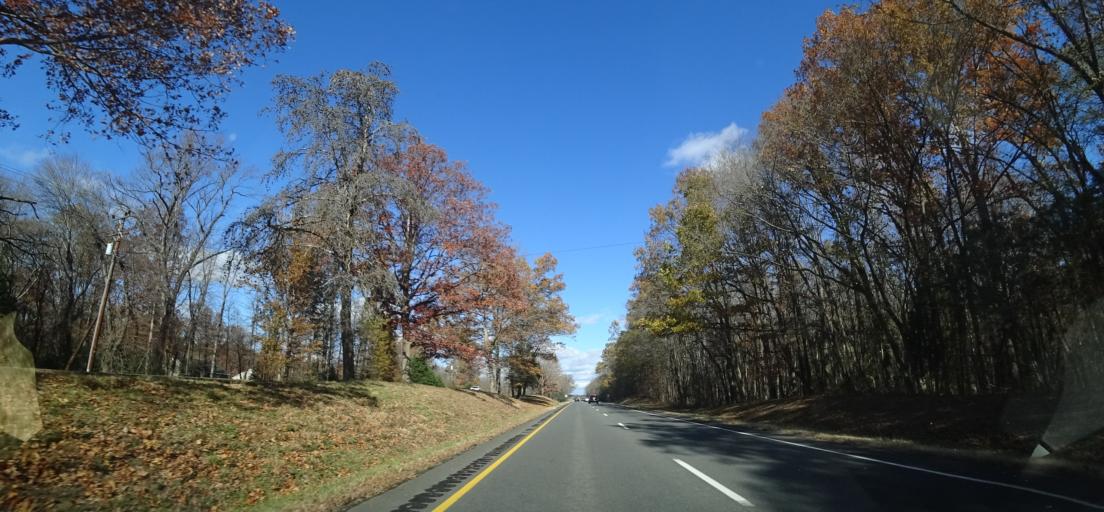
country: US
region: Virginia
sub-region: Fauquier County
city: Bealeton
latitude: 38.5934
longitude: -77.8013
